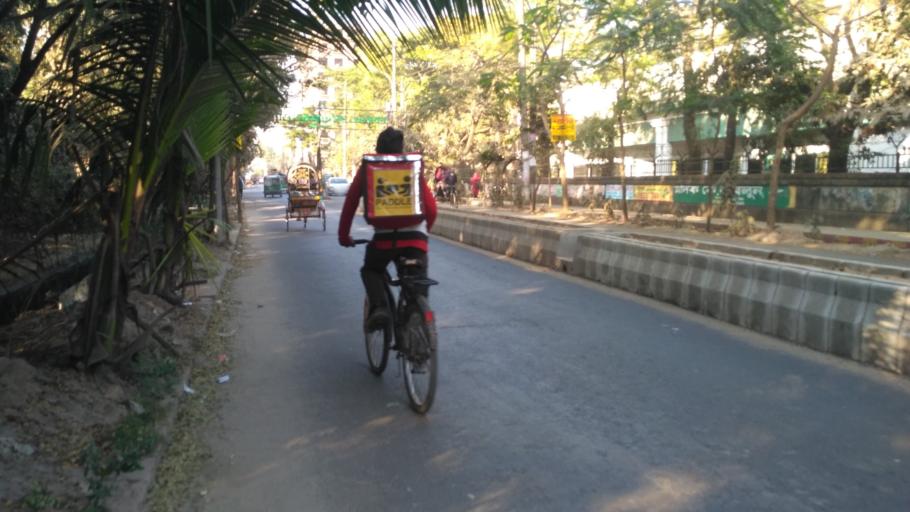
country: BD
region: Chittagong
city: Chittagong
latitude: 22.3750
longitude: 91.8470
